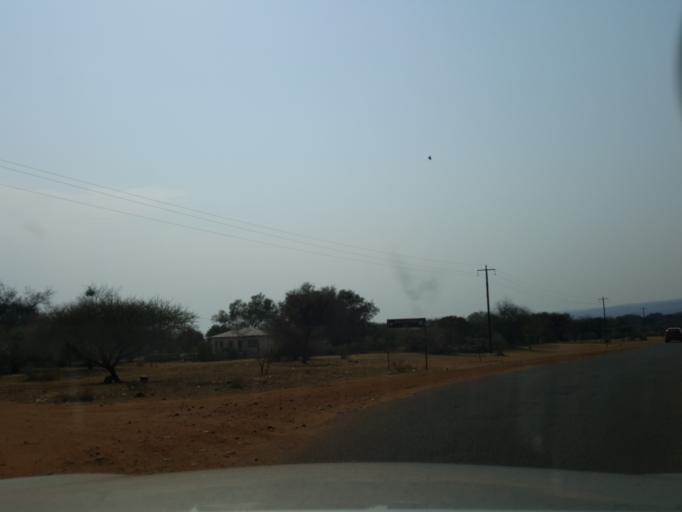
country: BW
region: South East
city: Lobatse
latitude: -25.2844
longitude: 25.9145
